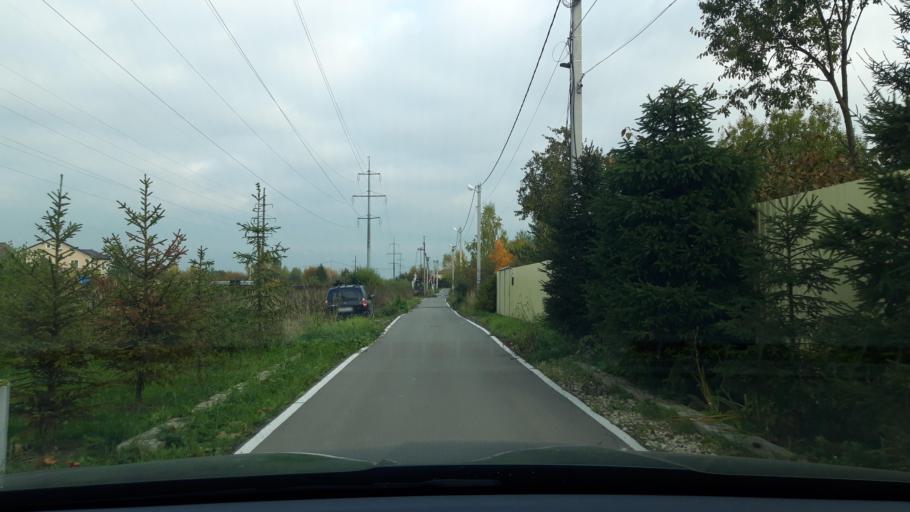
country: RU
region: Moskovskaya
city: Lozhki
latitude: 56.0621
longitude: 37.0913
